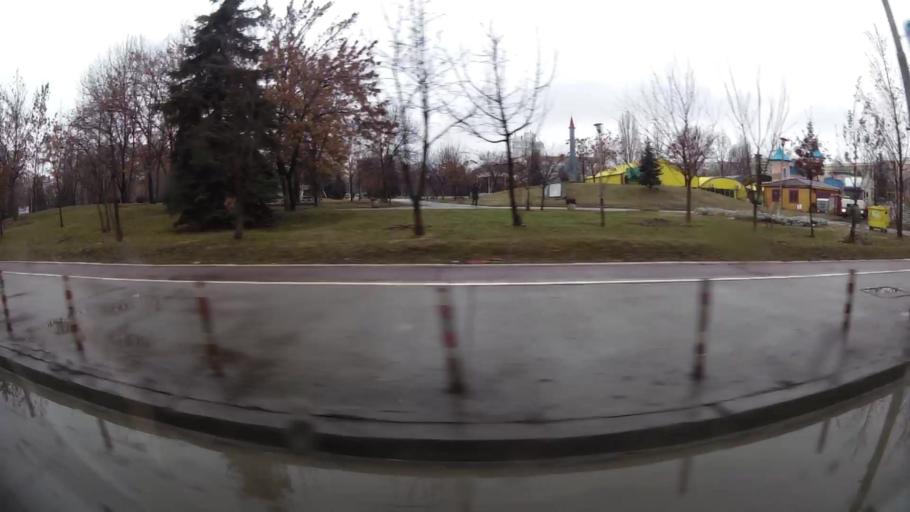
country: BG
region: Sofia-Capital
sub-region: Stolichna Obshtina
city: Sofia
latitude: 42.6423
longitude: 23.3806
